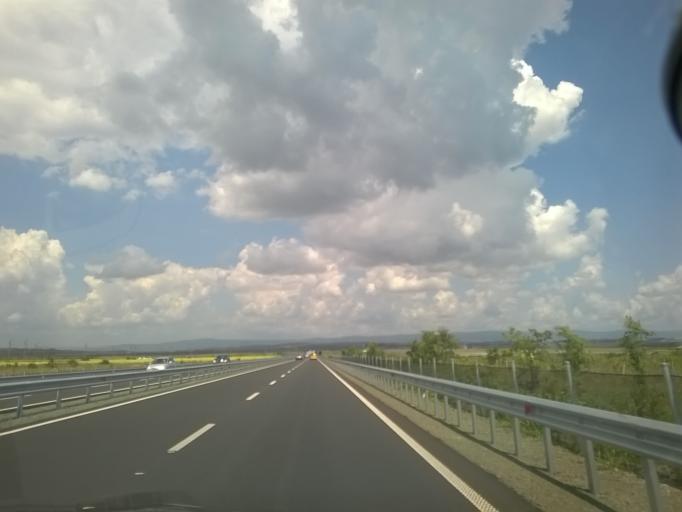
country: BG
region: Burgas
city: Aheloy
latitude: 42.6061
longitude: 27.6203
